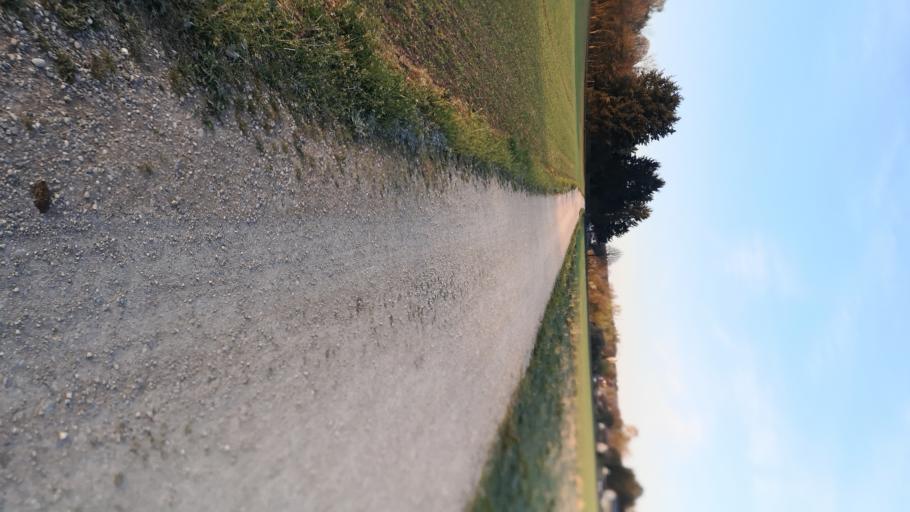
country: DE
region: Bavaria
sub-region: Upper Bavaria
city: Gauting
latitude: 48.0631
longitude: 11.4089
